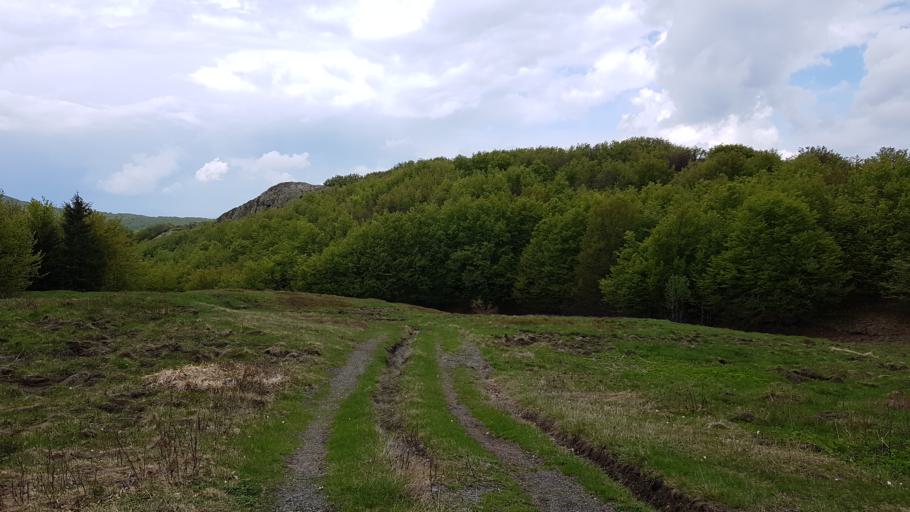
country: IT
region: Liguria
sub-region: Provincia di Genova
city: Santo Stefano d'Aveto
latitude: 44.5591
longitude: 9.4897
